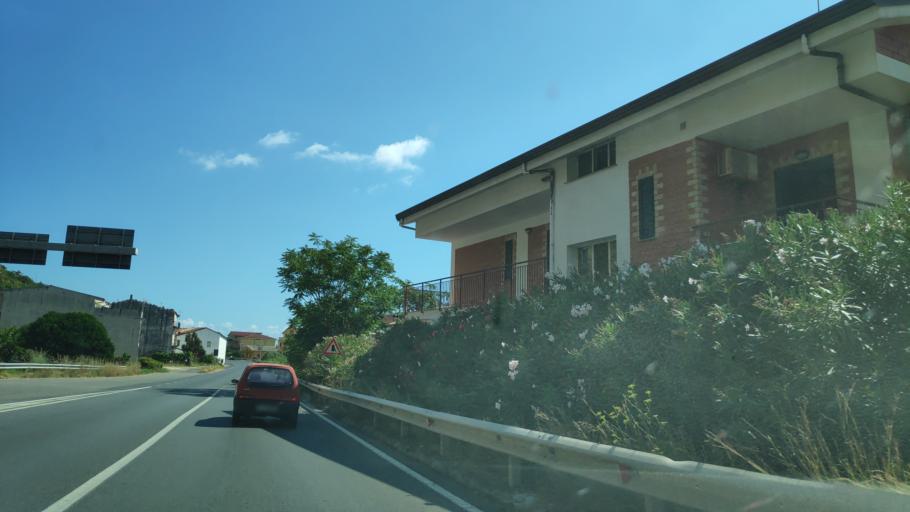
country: IT
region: Calabria
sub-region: Provincia di Cosenza
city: Campora San Giovanni
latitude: 39.0920
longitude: 16.0853
